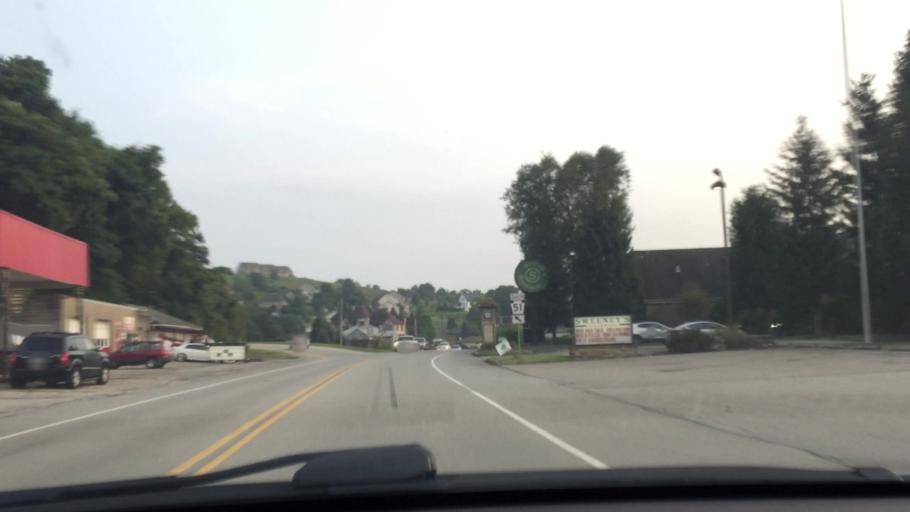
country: US
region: Pennsylvania
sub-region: Westmoreland County
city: Fellsburg
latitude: 40.1782
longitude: -79.8054
